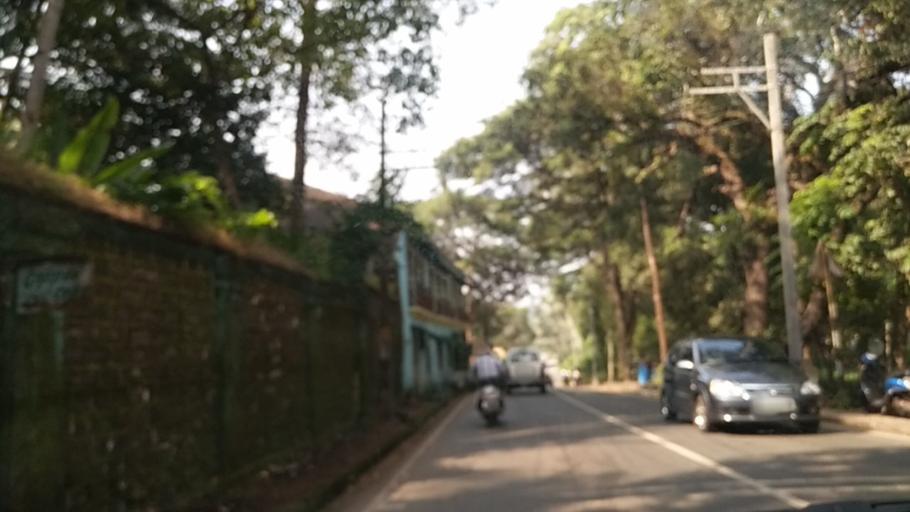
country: IN
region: Goa
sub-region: North Goa
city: Bambolim
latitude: 15.5000
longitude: 73.8945
